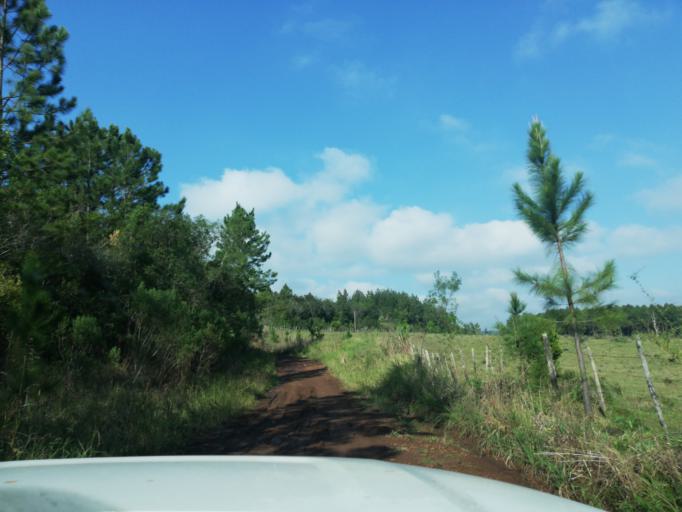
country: AR
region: Misiones
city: Cerro Azul
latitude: -27.5910
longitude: -55.5153
